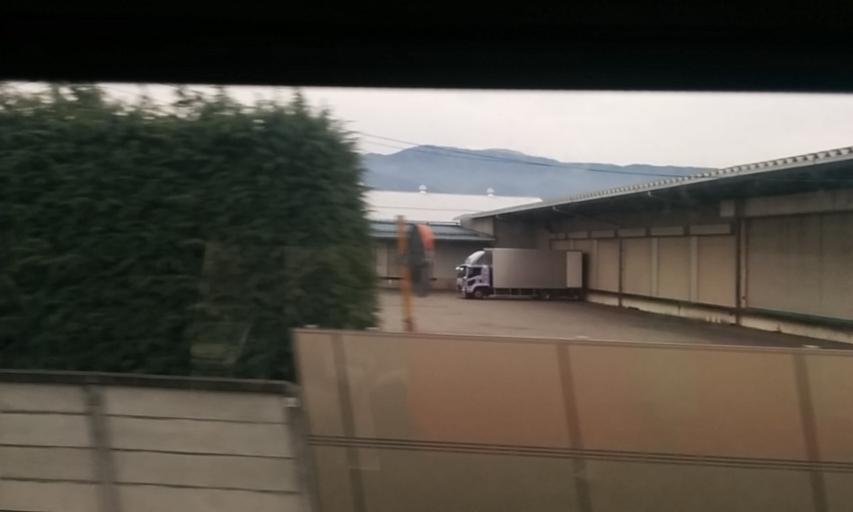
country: JP
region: Nagano
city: Matsumoto
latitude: 36.1891
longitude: 137.9618
